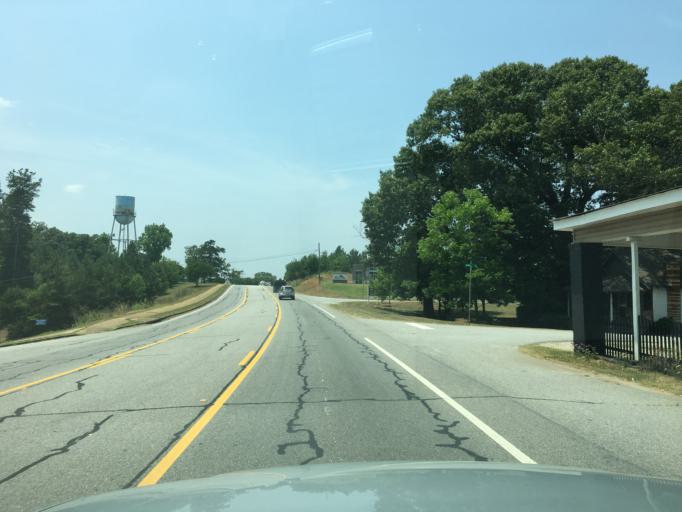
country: US
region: Georgia
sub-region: Hart County
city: Royston
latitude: 34.2851
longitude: -83.1443
